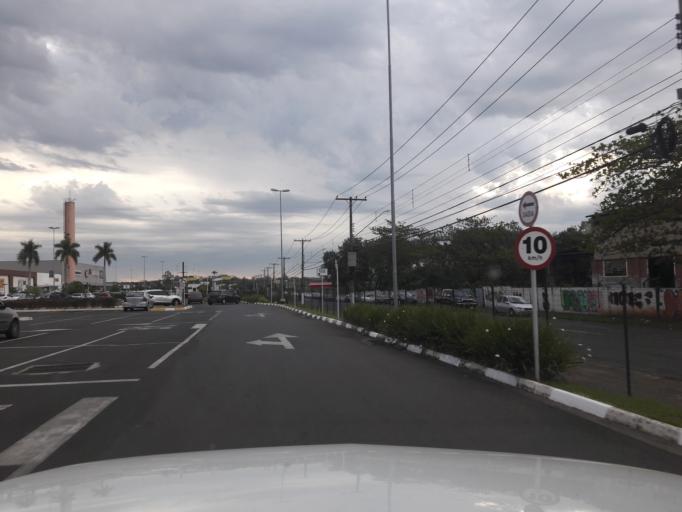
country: BR
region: Sao Paulo
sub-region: Moji-Guacu
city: Mogi-Gaucu
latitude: -22.3677
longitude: -46.9520
